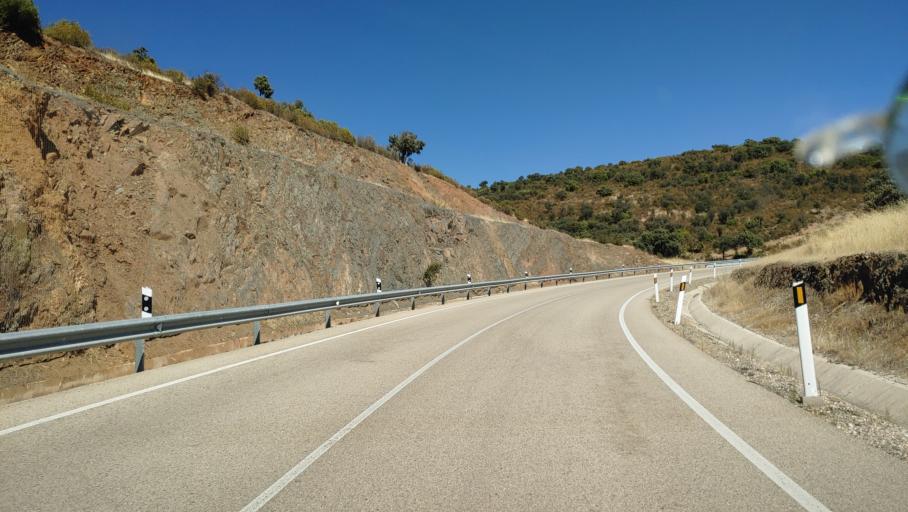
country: ES
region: Andalusia
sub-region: Provincia de Jaen
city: Genave
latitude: 38.4994
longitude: -2.7710
